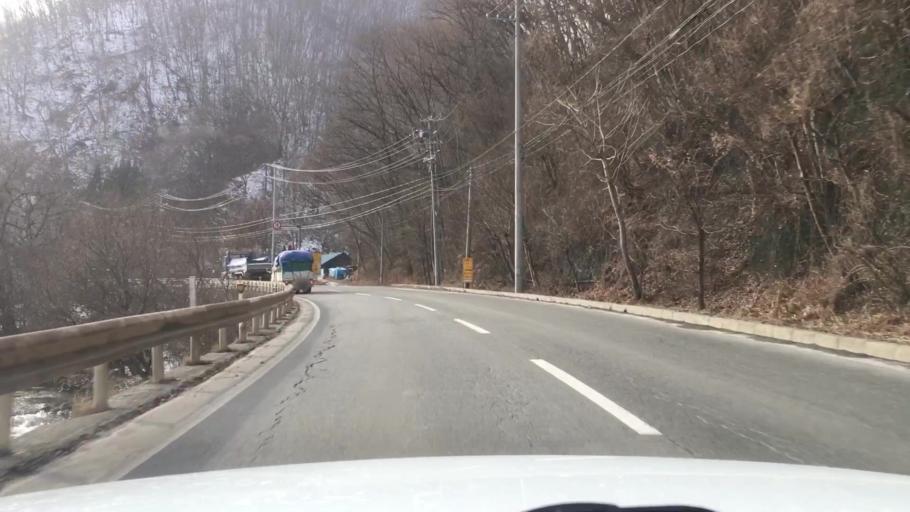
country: JP
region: Iwate
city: Tono
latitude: 39.6277
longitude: 141.5156
